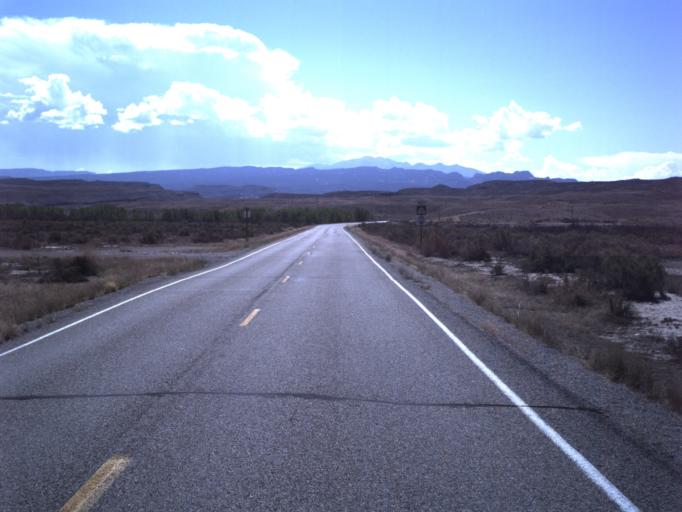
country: US
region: Utah
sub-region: Grand County
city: Moab
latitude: 38.8658
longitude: -109.2950
